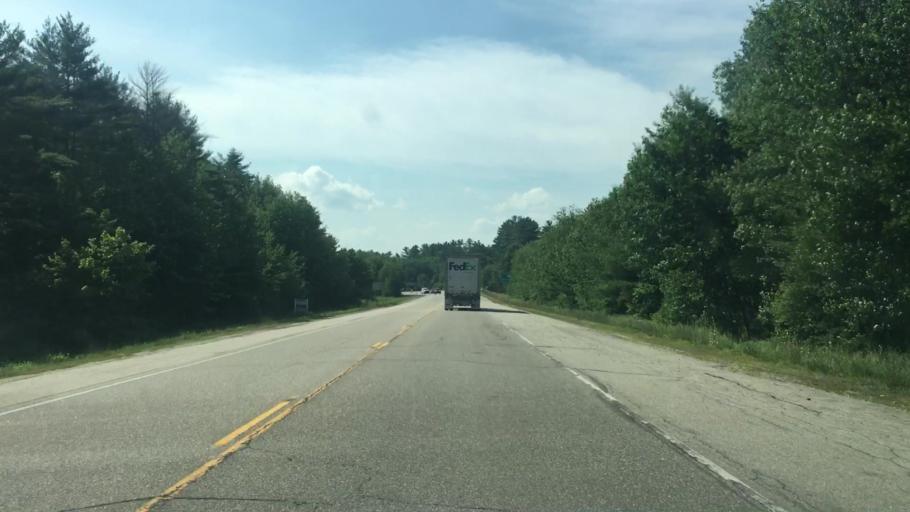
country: US
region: New Hampshire
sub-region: Strafford County
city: Rochester
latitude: 43.3287
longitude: -70.9677
